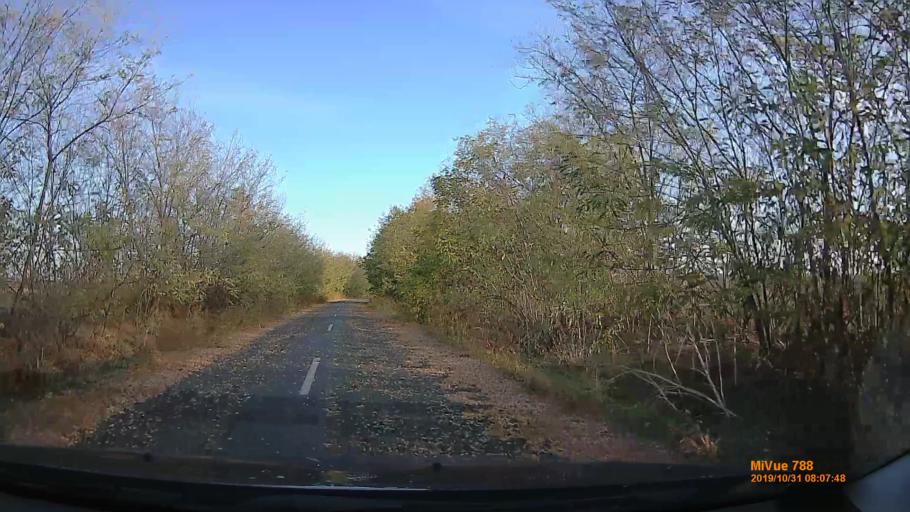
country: HU
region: Pest
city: Pilis
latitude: 47.3097
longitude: 19.5633
